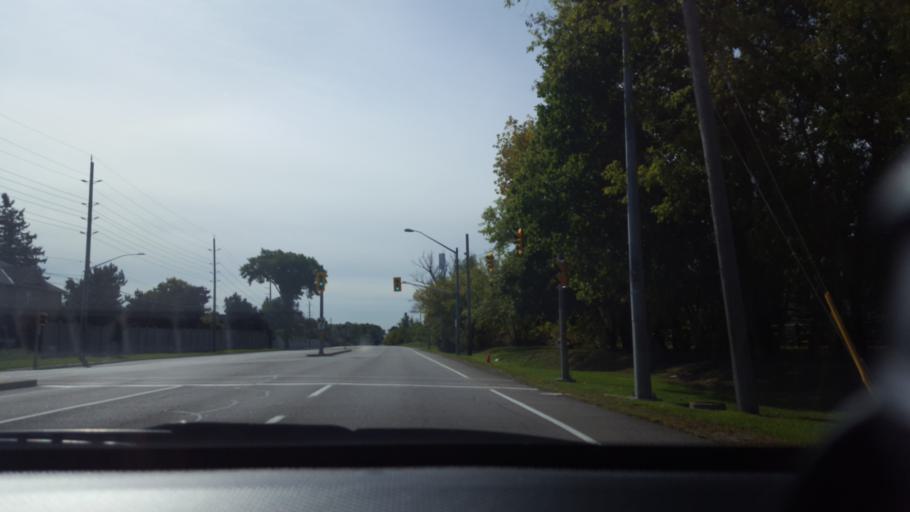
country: CA
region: Ontario
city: Newmarket
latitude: 43.9894
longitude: -79.4932
